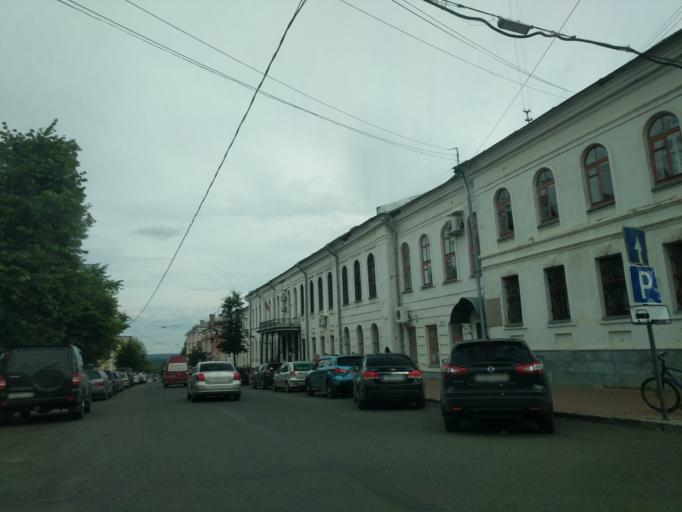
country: RU
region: Kirov
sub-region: Kirovo-Chepetskiy Rayon
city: Kirov
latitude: 58.6020
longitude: 49.6723
